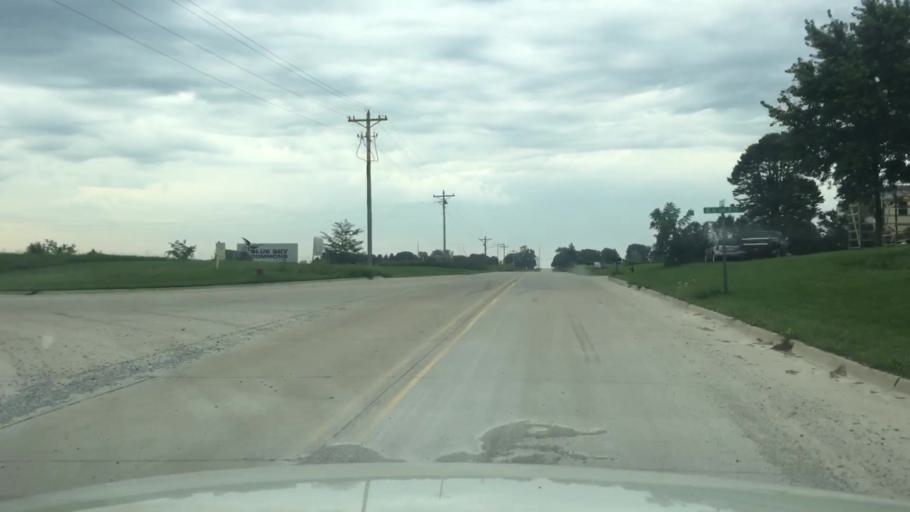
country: US
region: Iowa
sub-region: Story County
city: Huxley
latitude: 41.8859
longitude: -93.5810
